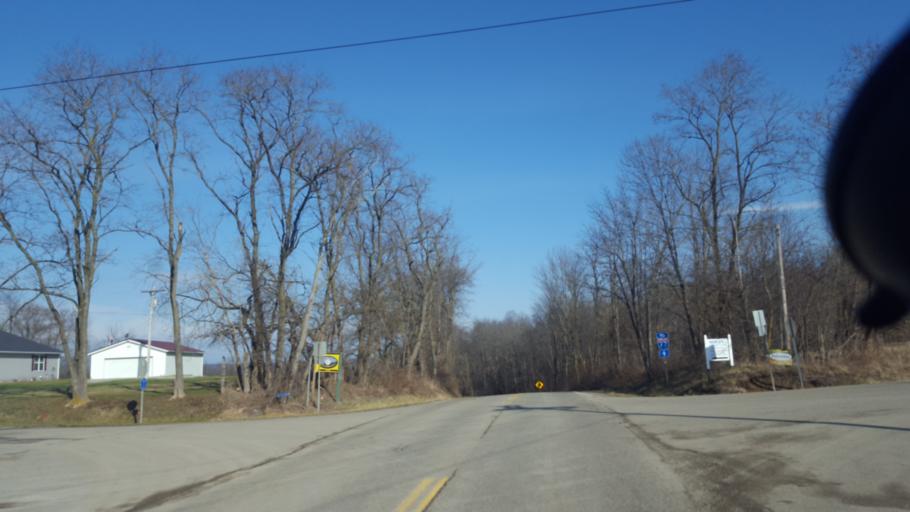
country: US
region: Ohio
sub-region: Tuscarawas County
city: Newcomerstown
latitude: 40.2308
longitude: -81.5042
